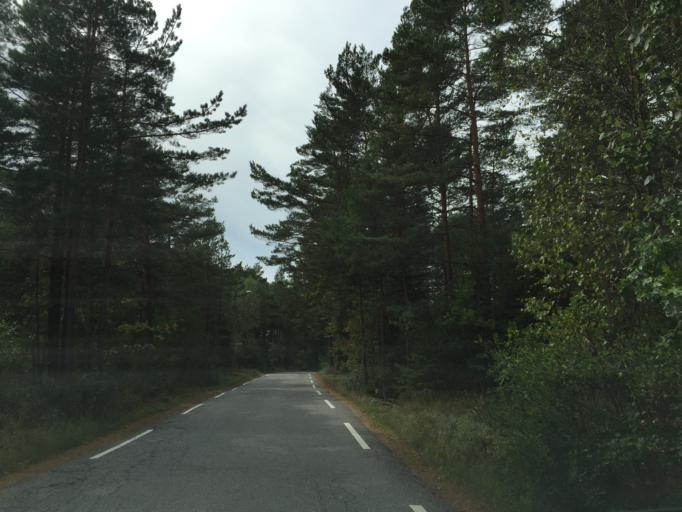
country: NO
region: Ostfold
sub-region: Fredrikstad
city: Fredrikstad
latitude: 59.0971
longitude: 10.9319
